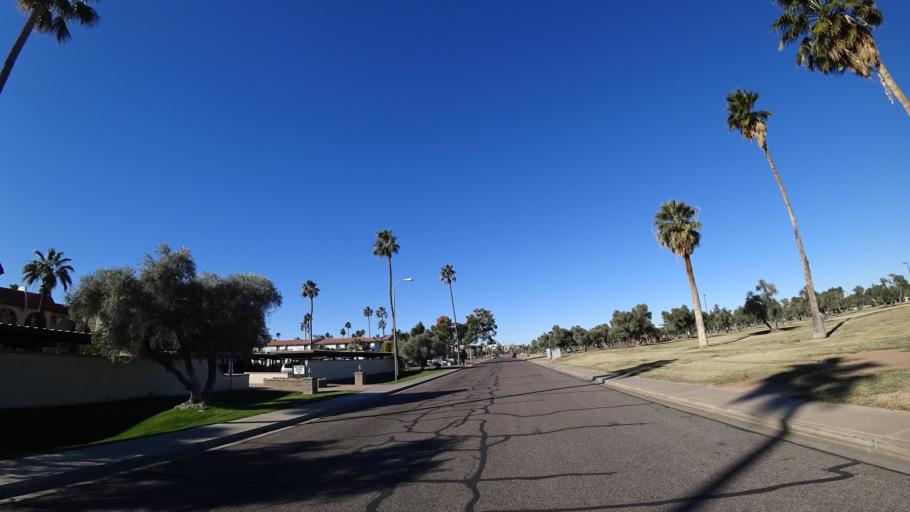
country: US
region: Arizona
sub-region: Maricopa County
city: Phoenix
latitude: 33.4970
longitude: -112.0167
